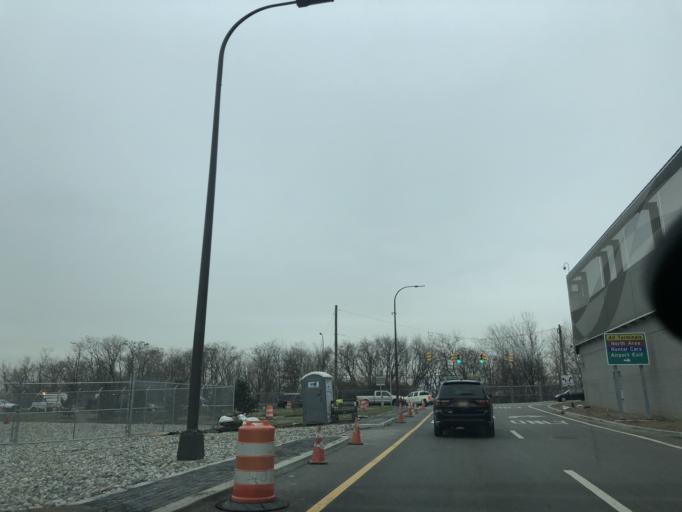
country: US
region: New Jersey
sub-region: Union County
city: Elizabeth
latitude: 40.6818
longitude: -74.1911
